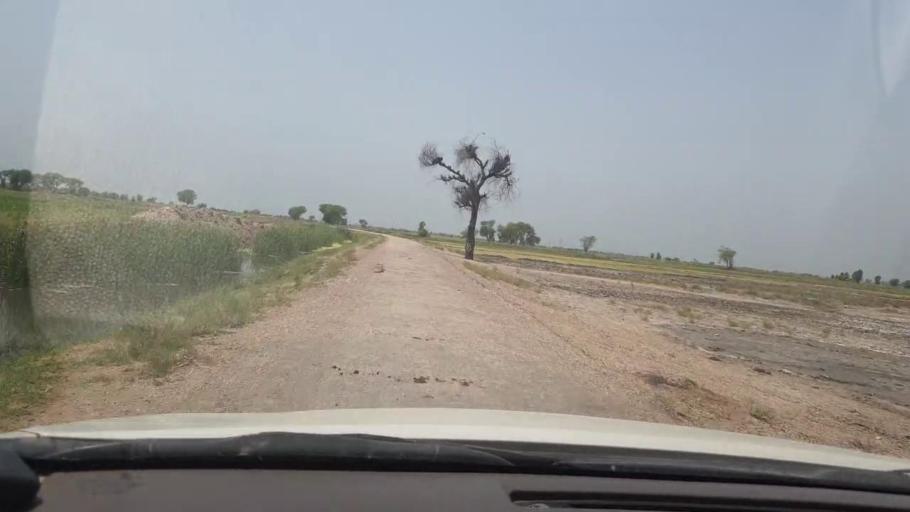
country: PK
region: Sindh
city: Garhi Yasin
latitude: 27.9061
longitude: 68.5434
